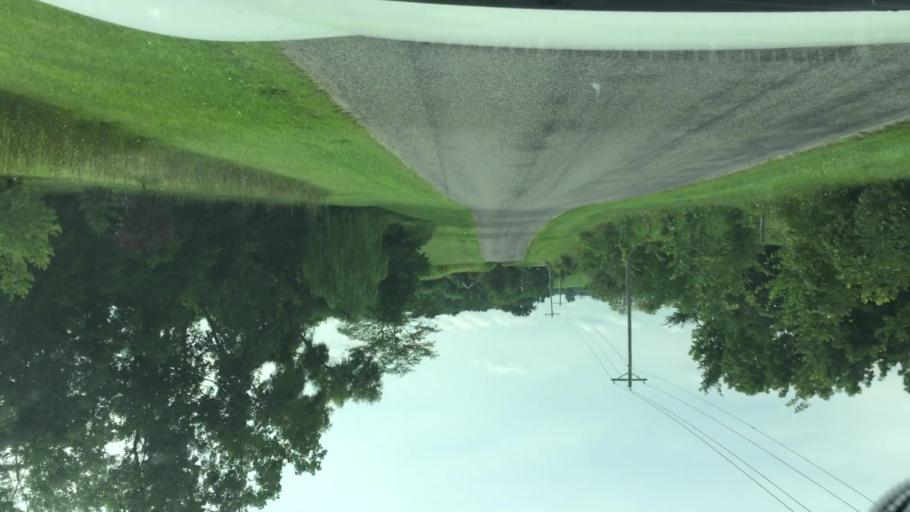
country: US
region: Ohio
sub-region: Champaign County
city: Mechanicsburg
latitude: 40.0541
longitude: -83.5764
